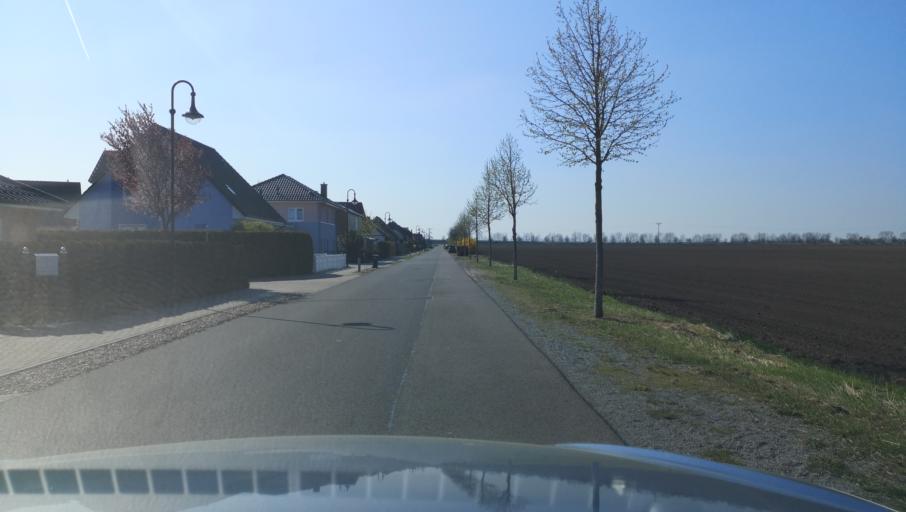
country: DE
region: Saxony-Anhalt
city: Barleben
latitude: 52.2108
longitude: 11.6167
